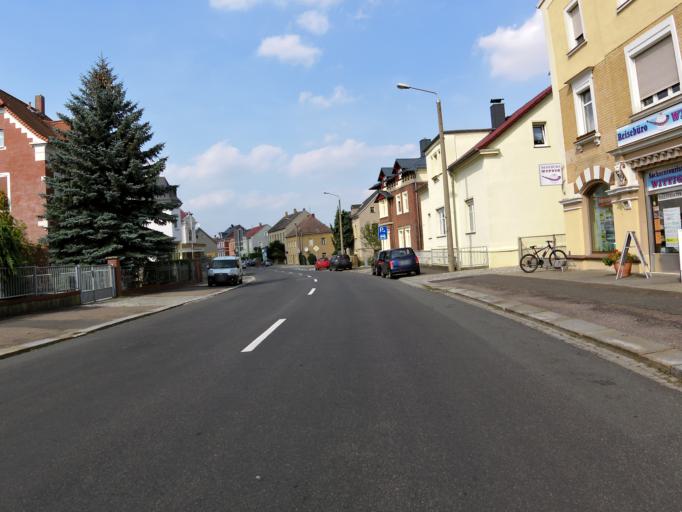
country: DE
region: Saxony
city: Oschatz
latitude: 51.3029
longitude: 13.1083
